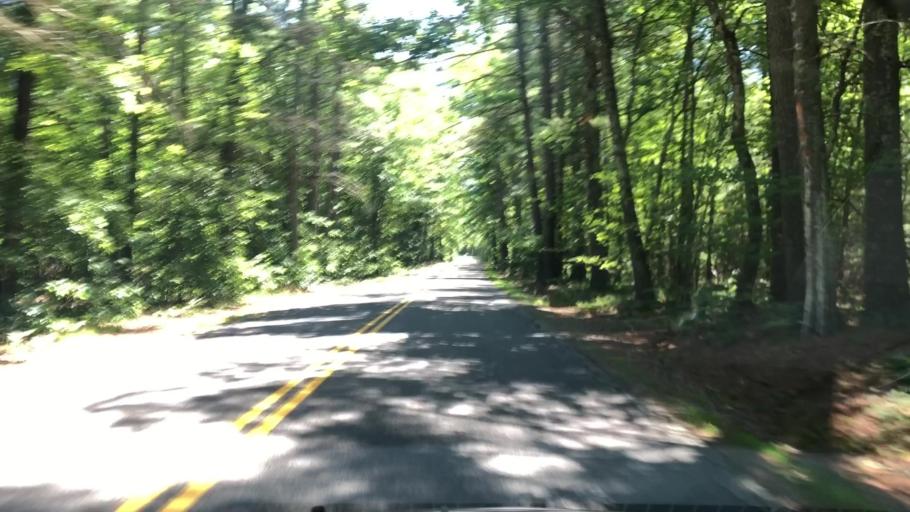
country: US
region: New Hampshire
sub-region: Hillsborough County
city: Milford
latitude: 42.8406
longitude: -71.5733
